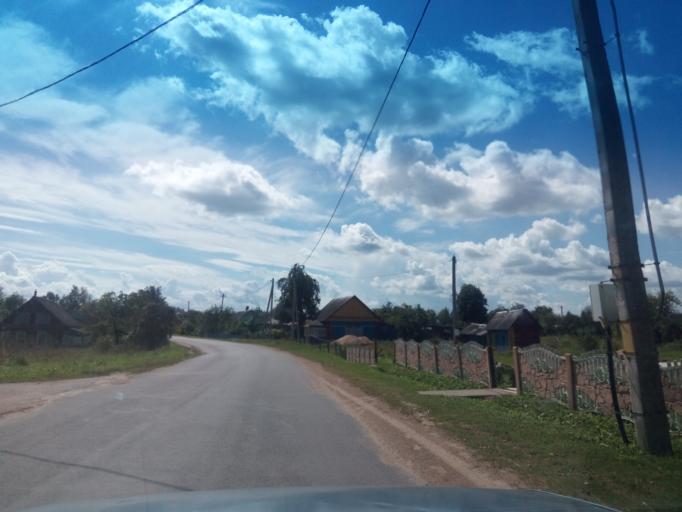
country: BY
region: Vitebsk
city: Dzisna
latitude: 55.6666
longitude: 28.3271
